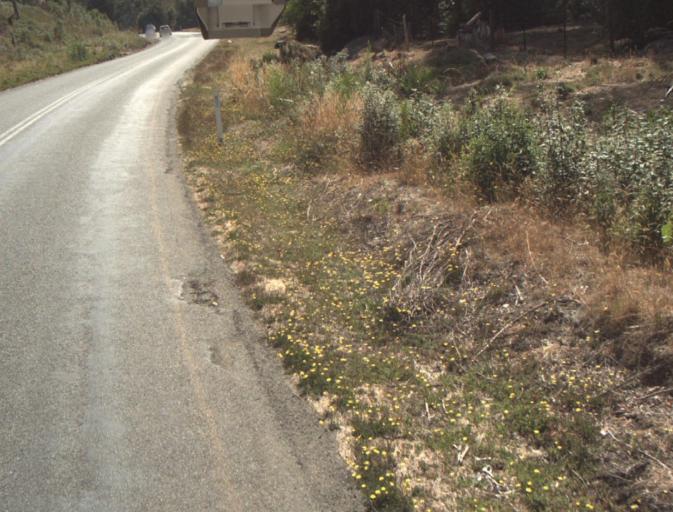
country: AU
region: Tasmania
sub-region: Launceston
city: Mayfield
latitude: -41.2045
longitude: 147.2156
